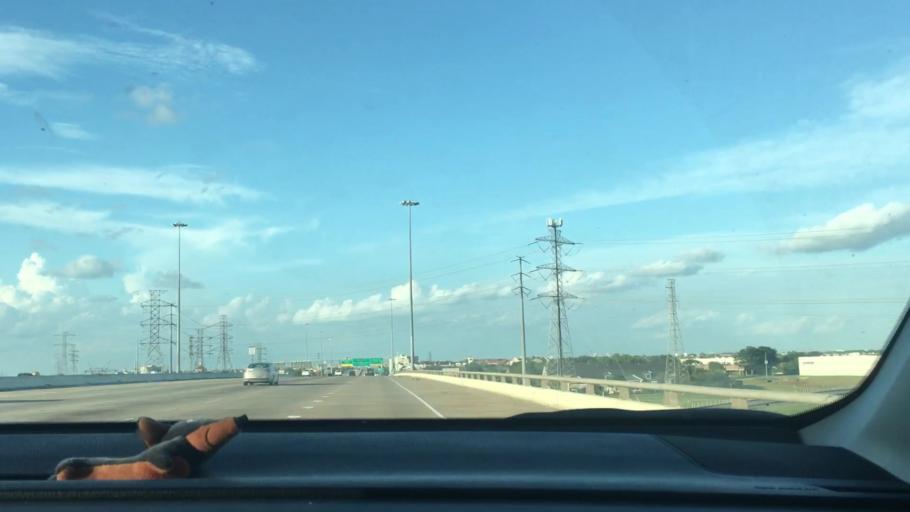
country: US
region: Texas
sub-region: Fort Bend County
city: Meadows Place
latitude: 29.6282
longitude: -95.5930
